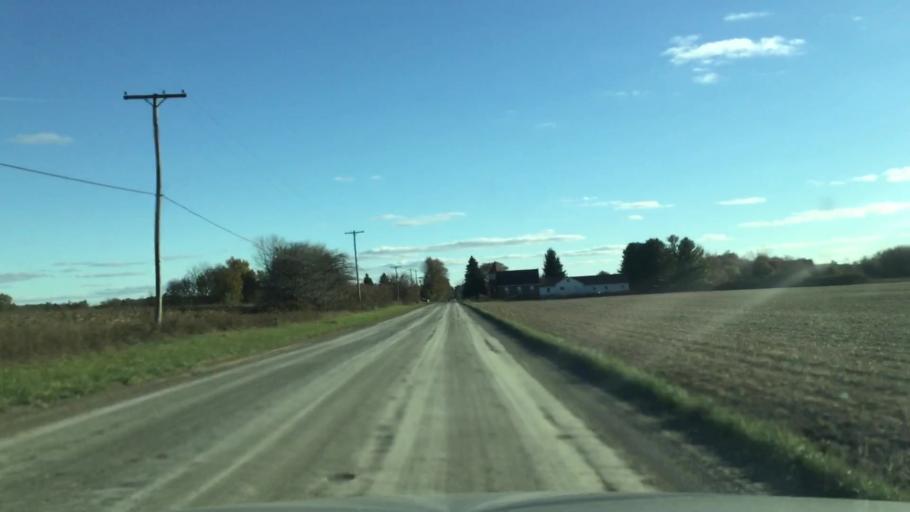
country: US
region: Michigan
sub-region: Lapeer County
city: Lapeer
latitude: 43.0704
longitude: -83.2273
